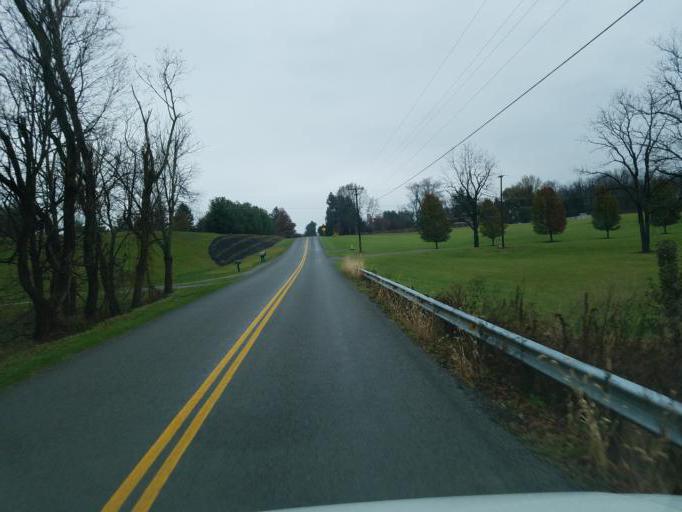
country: US
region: Ohio
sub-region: Richland County
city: Ontario
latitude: 40.7192
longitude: -82.5991
